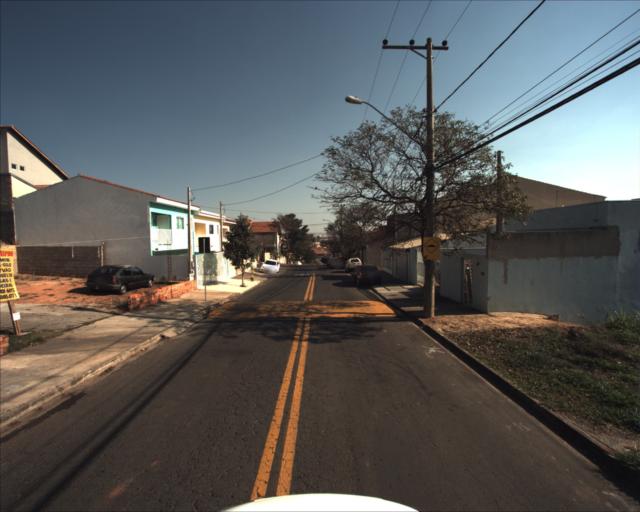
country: BR
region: Sao Paulo
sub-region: Sorocaba
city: Sorocaba
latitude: -23.4983
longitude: -47.4247
